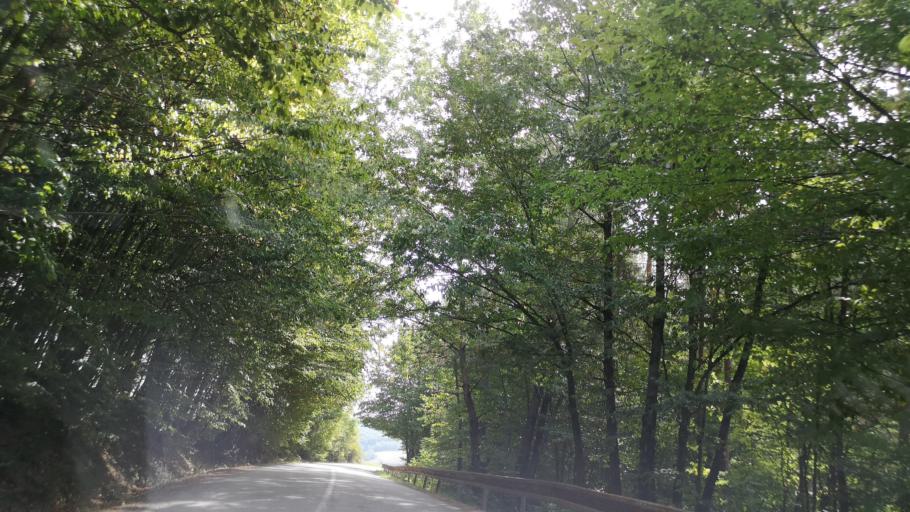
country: SK
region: Banskobystricky
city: Revuca
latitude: 48.6060
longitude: 20.1635
